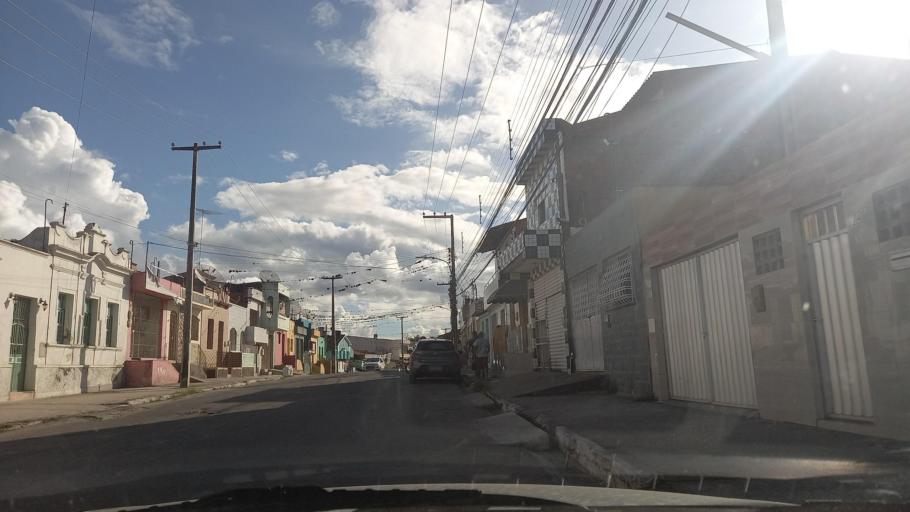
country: BR
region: Pernambuco
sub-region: Gravata
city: Gravata
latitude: -8.2043
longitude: -35.5750
